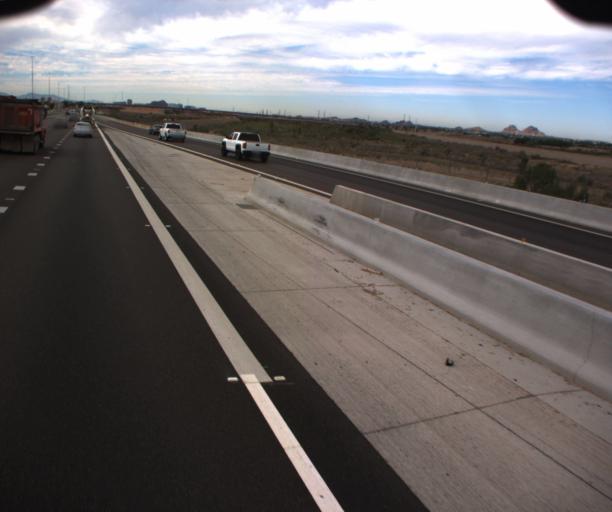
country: US
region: Arizona
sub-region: Maricopa County
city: Tempe
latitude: 33.4371
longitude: -111.8722
